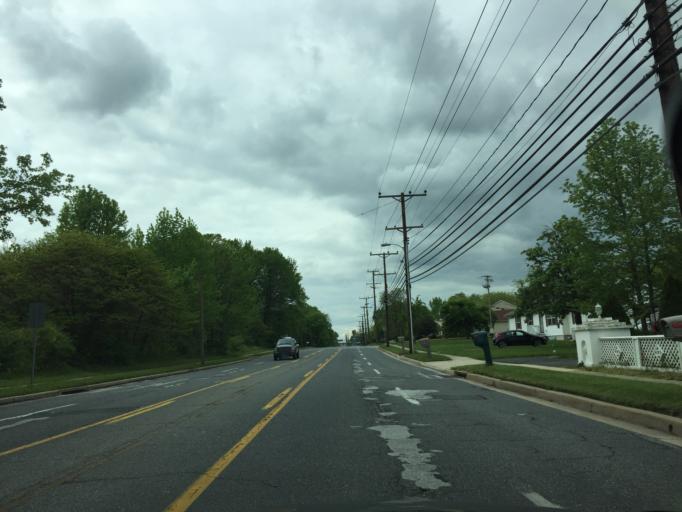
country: US
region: Maryland
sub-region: Baltimore County
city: Middle River
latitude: 39.3015
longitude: -76.4383
